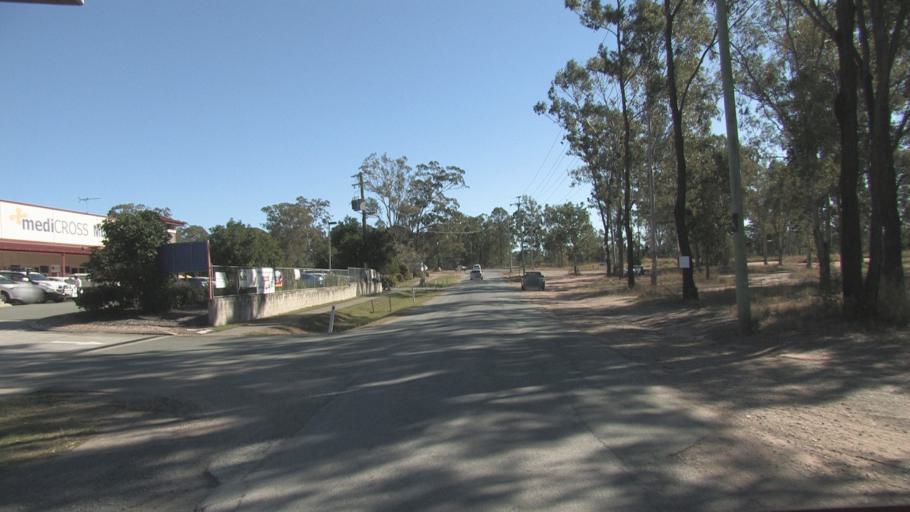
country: AU
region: Queensland
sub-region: Logan
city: North Maclean
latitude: -27.7679
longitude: 153.0190
